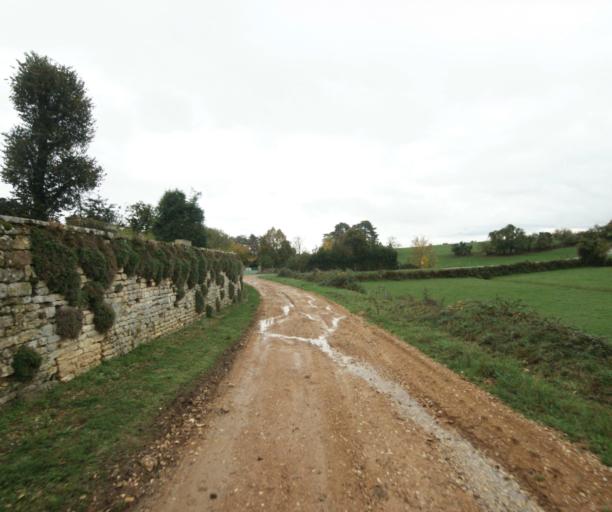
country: FR
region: Rhone-Alpes
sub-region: Departement de l'Ain
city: Pont-de-Vaux
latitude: 46.4838
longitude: 4.8637
